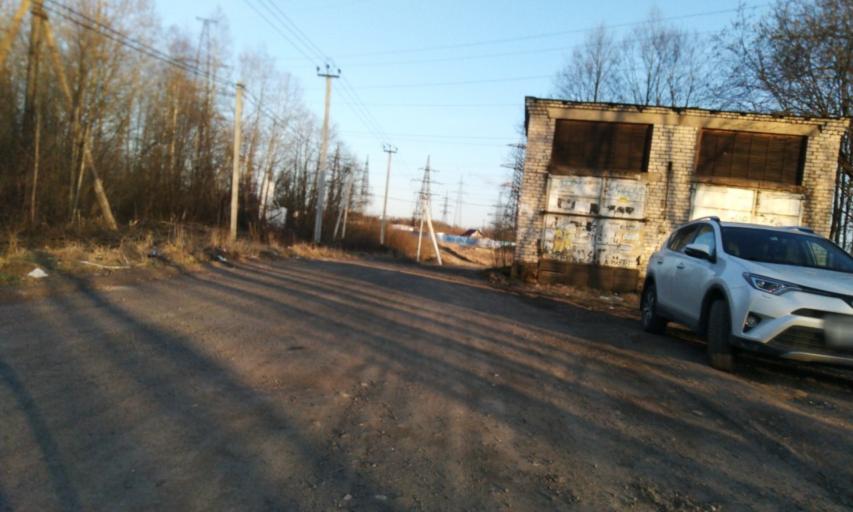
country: RU
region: Leningrad
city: Novoye Devyatkino
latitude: 60.0912
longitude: 30.4590
